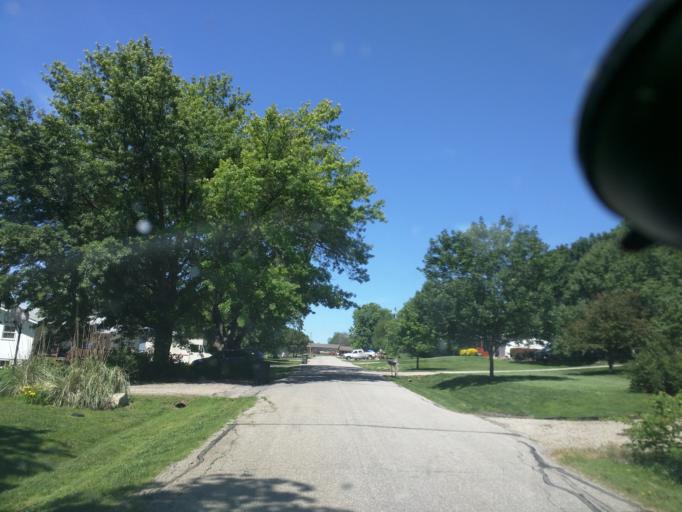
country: US
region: Kansas
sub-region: Riley County
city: Manhattan
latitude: 39.2162
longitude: -96.6136
